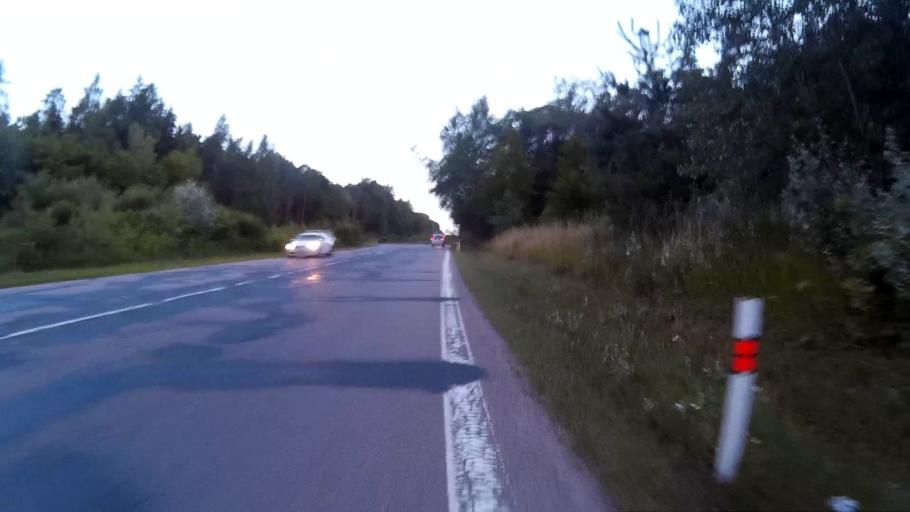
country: CZ
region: South Moravian
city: Troubsko
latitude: 49.1992
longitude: 16.5151
